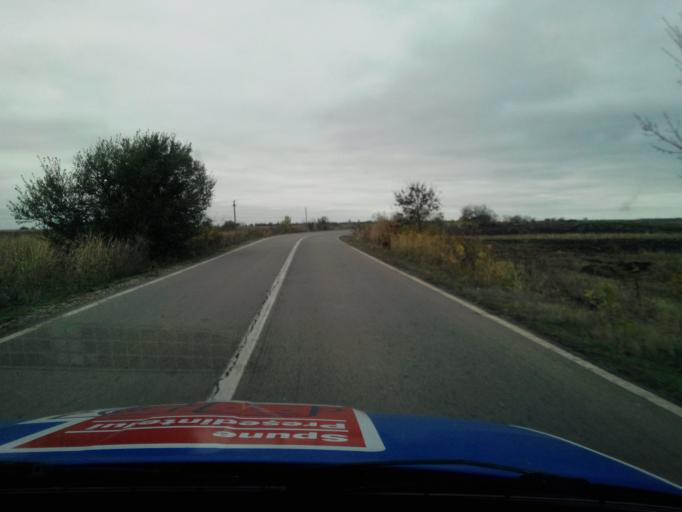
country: RO
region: Giurgiu
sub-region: Comuna Baneasa
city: Pietrele
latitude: 44.0764
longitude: 26.1368
